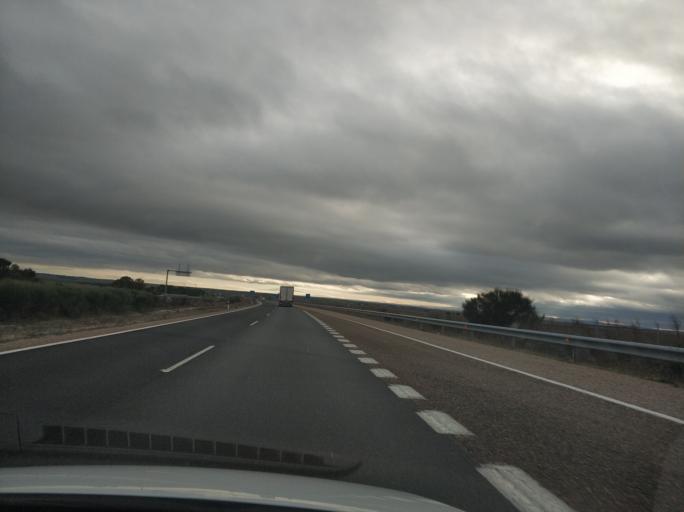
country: ES
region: Castille and Leon
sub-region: Provincia de Salamanca
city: Aldeanueva de Figueroa
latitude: 41.1326
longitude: -5.4894
